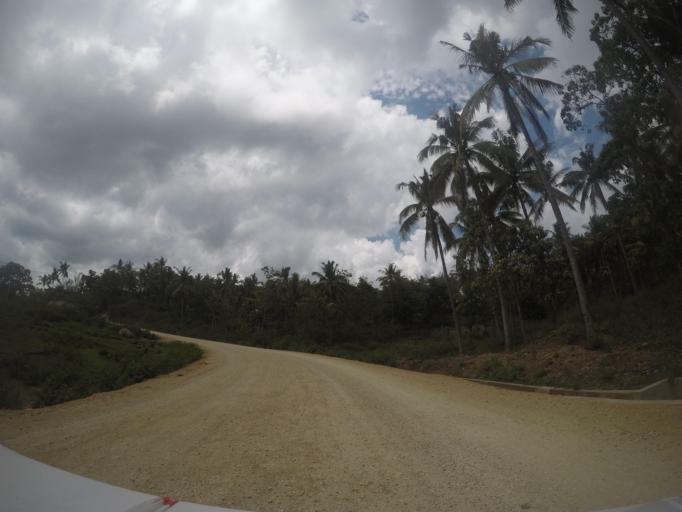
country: TL
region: Baucau
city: Baucau
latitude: -8.5331
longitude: 126.4249
